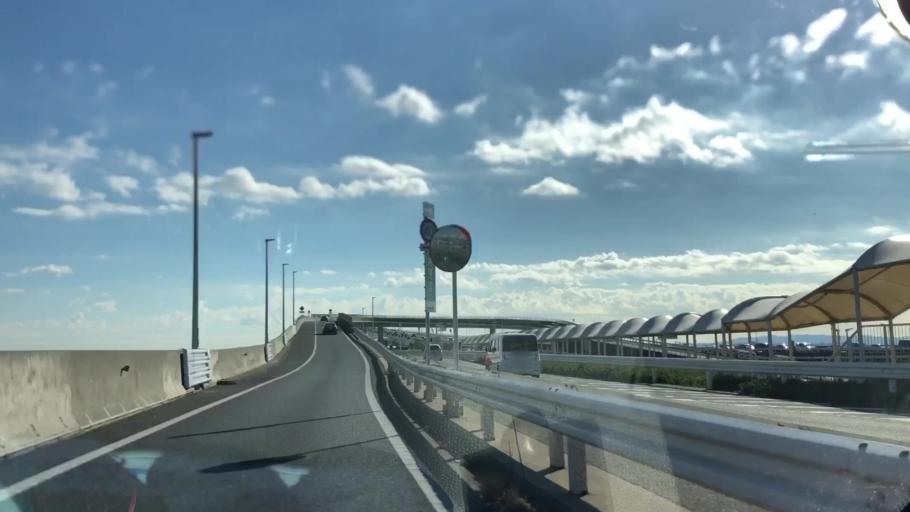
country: JP
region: Chiba
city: Kisarazu
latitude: 35.4636
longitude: 139.8763
